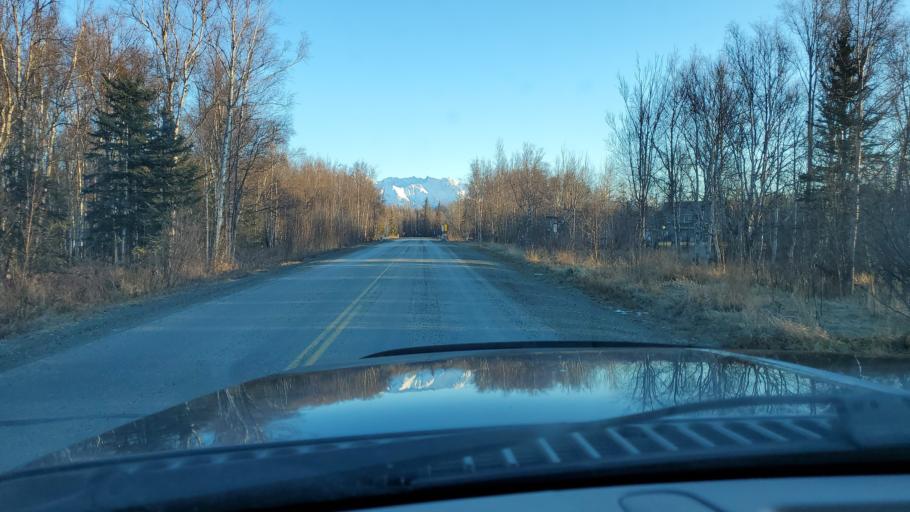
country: US
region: Alaska
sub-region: Matanuska-Susitna Borough
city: Gateway
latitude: 61.5885
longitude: -149.2536
